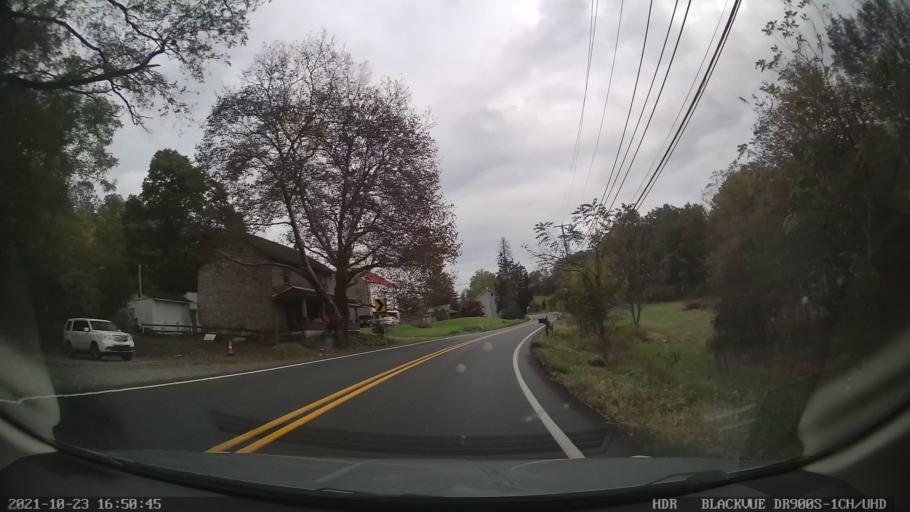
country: US
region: Pennsylvania
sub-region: Berks County
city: Red Lion
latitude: 40.4762
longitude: -75.6118
